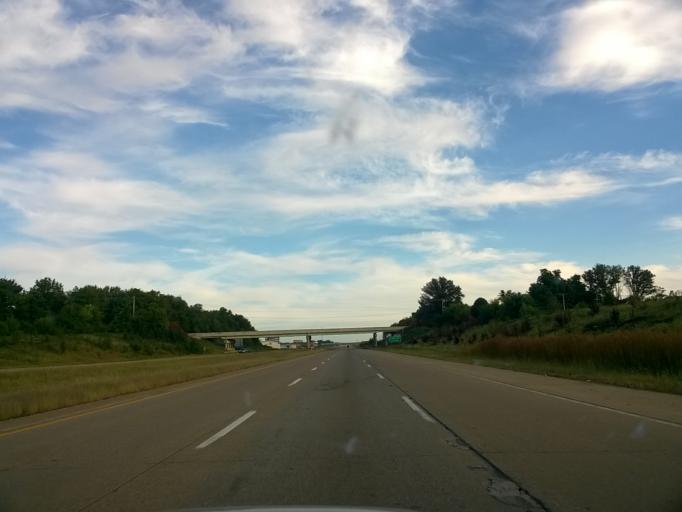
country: US
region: Indiana
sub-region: Vanderburgh County
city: Melody Hill
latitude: 38.0039
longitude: -87.4672
